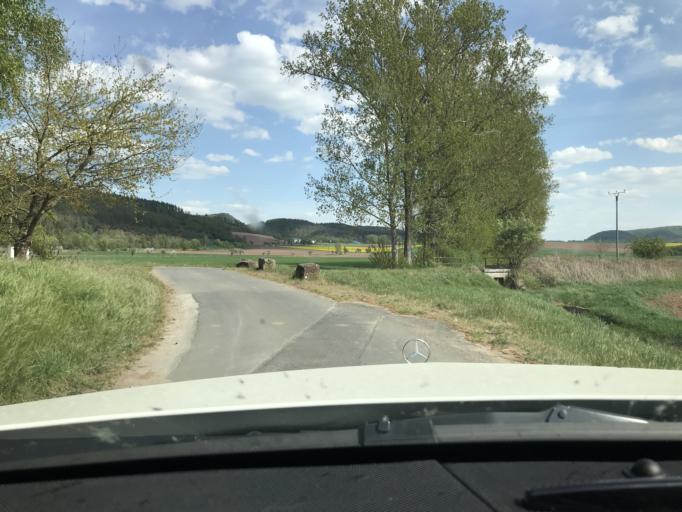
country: DE
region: Hesse
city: Wanfried
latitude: 51.1466
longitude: 10.1828
